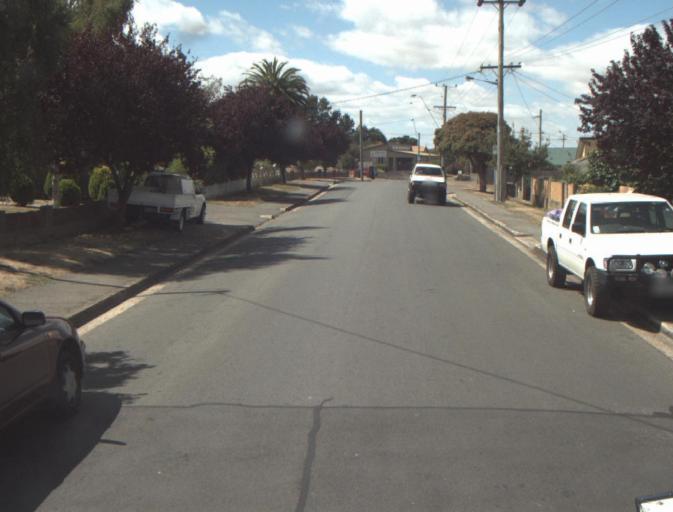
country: AU
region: Tasmania
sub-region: Launceston
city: Newstead
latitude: -41.4206
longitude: 147.1670
